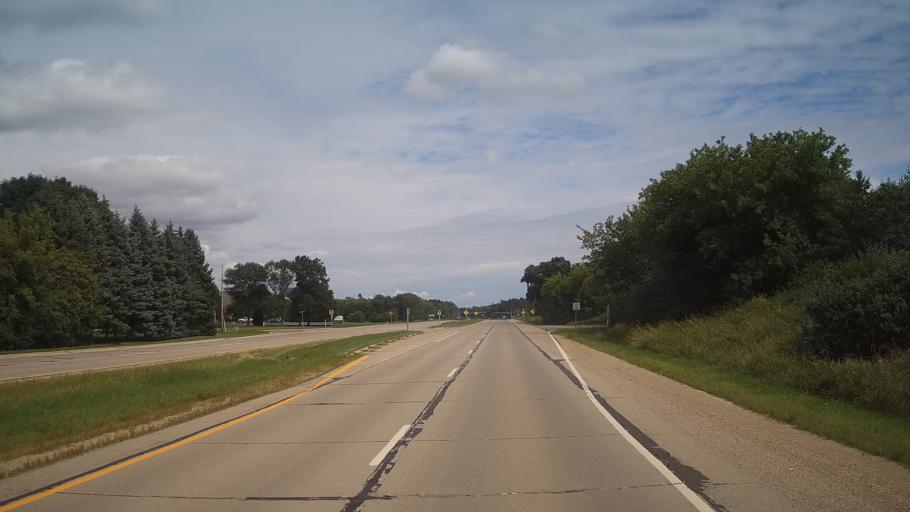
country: US
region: Wisconsin
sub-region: Winnebago County
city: Oshkosh
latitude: 44.0290
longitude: -88.6114
